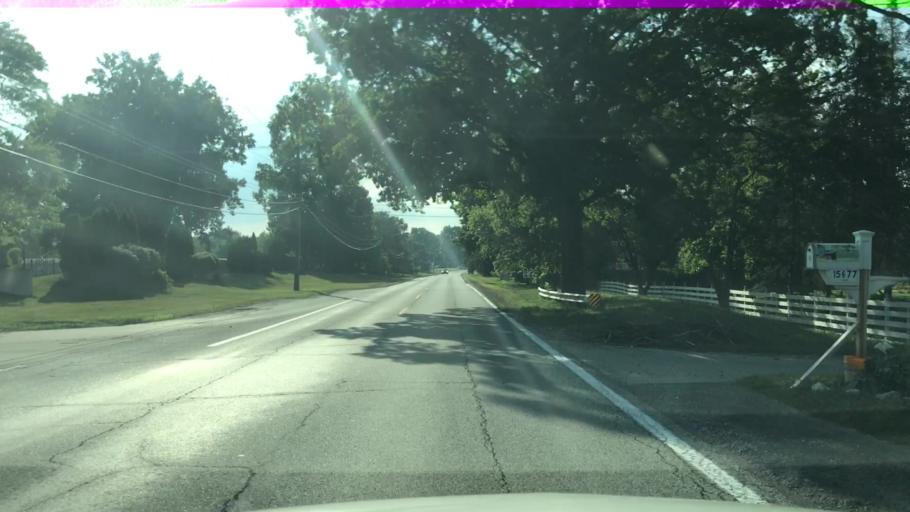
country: US
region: Michigan
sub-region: Macomb County
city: Fraser
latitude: 42.5779
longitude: -82.9656
